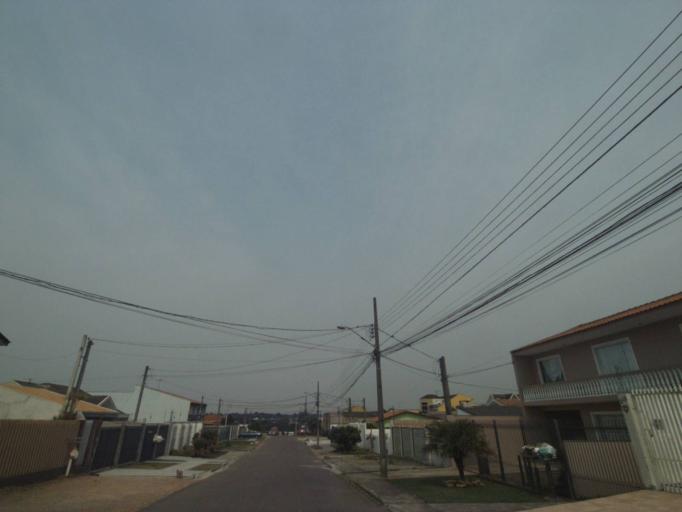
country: BR
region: Parana
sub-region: Sao Jose Dos Pinhais
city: Sao Jose dos Pinhais
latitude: -25.5194
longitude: -49.2792
